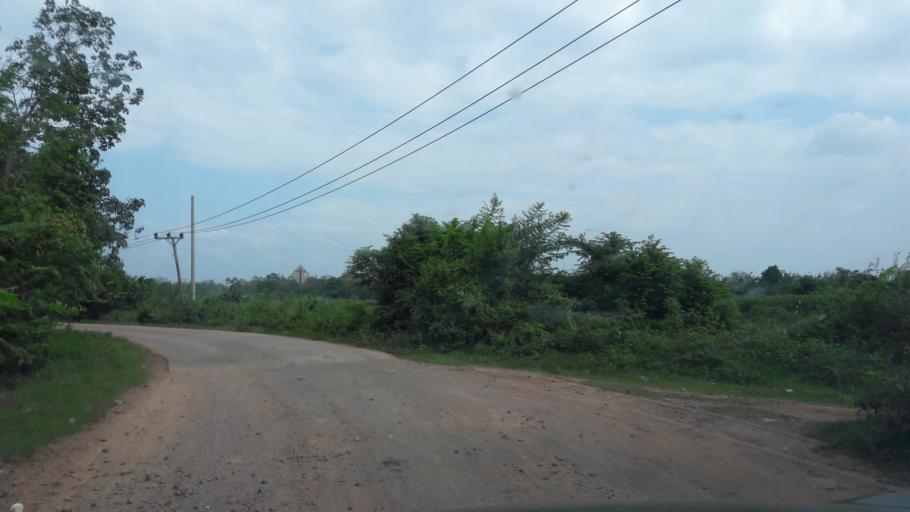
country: ID
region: South Sumatra
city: Prabumulih
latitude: -3.3205
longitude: 104.1233
